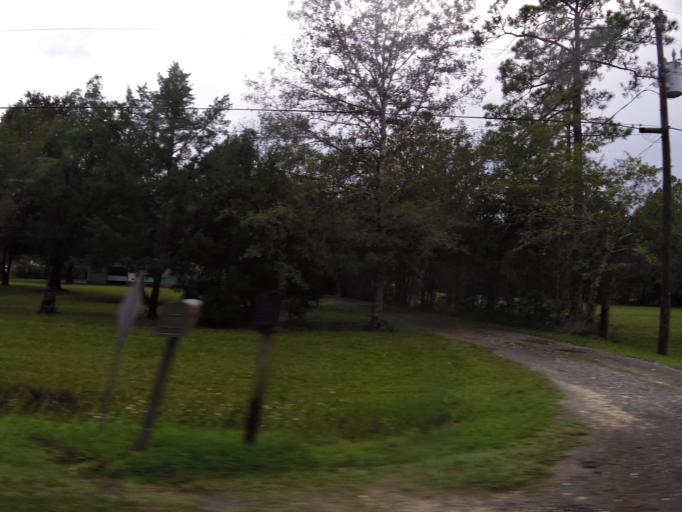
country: US
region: Florida
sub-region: Duval County
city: Baldwin
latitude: 30.3939
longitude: -81.9451
